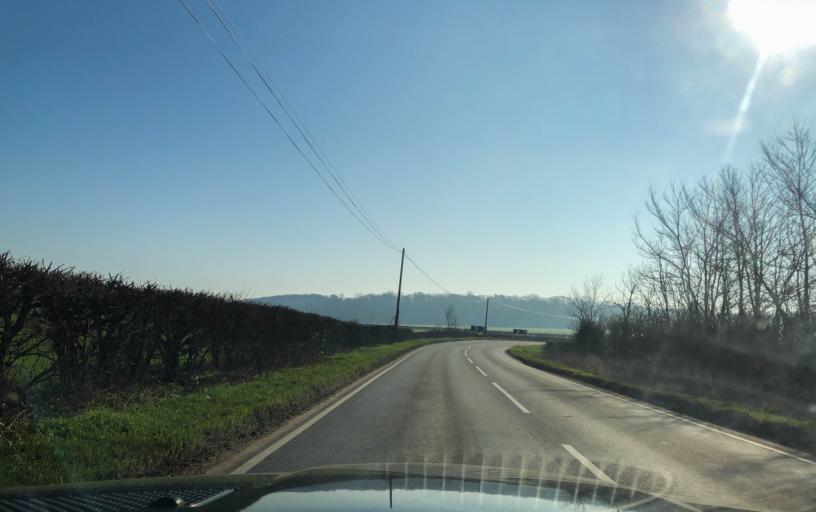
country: GB
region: England
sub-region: Warwickshire
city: Wellesbourne Mountford
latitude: 52.1874
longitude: -1.5811
